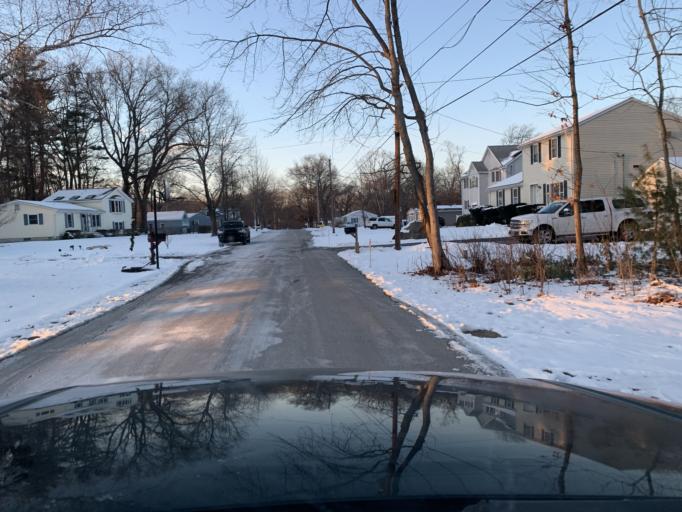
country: US
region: Massachusetts
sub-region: Essex County
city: Haverhill
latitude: 42.7905
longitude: -71.1119
